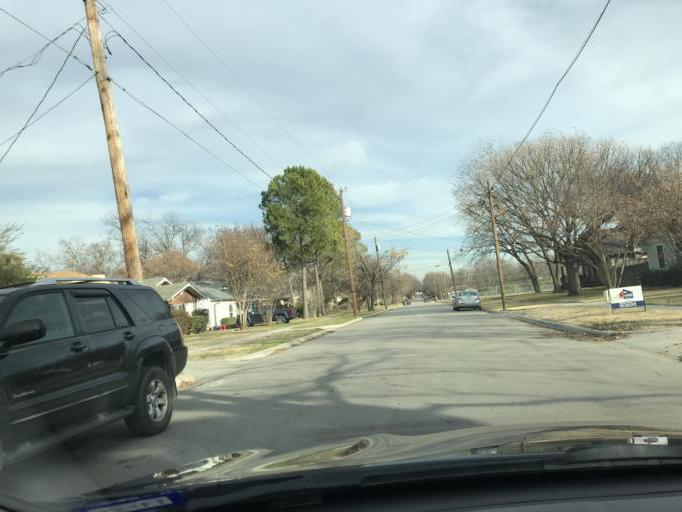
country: US
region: Texas
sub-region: Denton County
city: Denton
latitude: 33.2204
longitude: -97.1412
